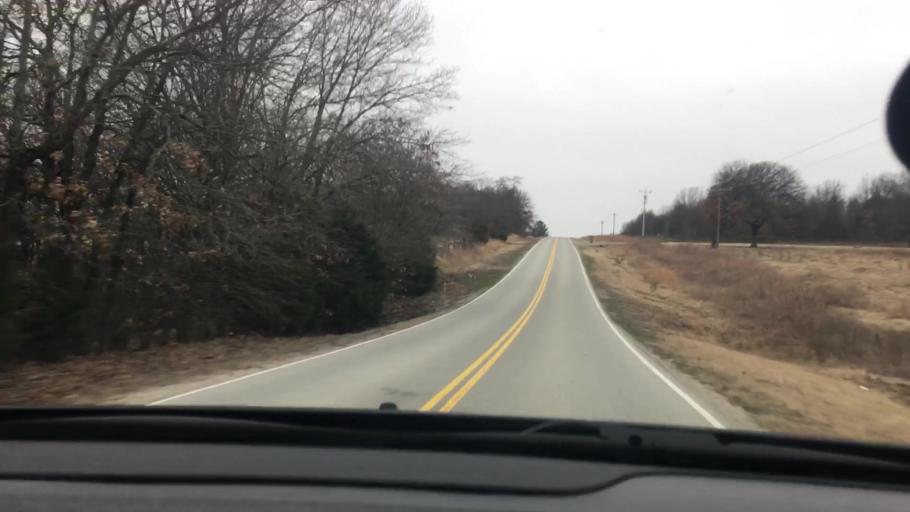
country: US
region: Oklahoma
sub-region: Coal County
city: Coalgate
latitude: 34.5055
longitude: -96.3350
